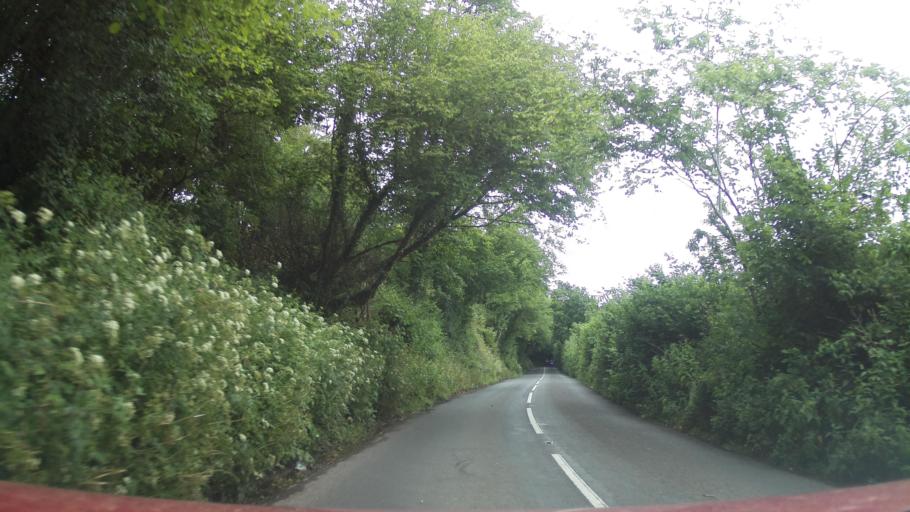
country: GB
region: England
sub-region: Devon
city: Chudleigh
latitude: 50.6416
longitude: -3.6368
